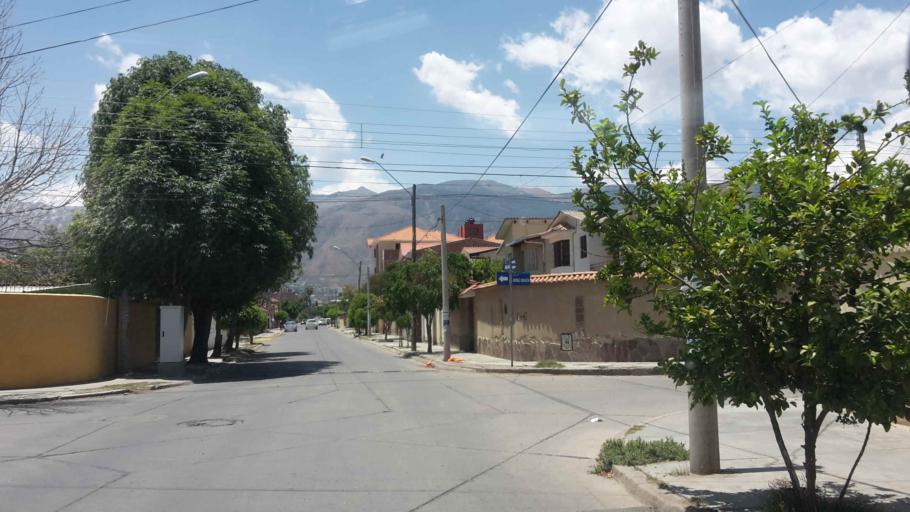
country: BO
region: Cochabamba
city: Cochabamba
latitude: -17.3796
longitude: -66.1913
